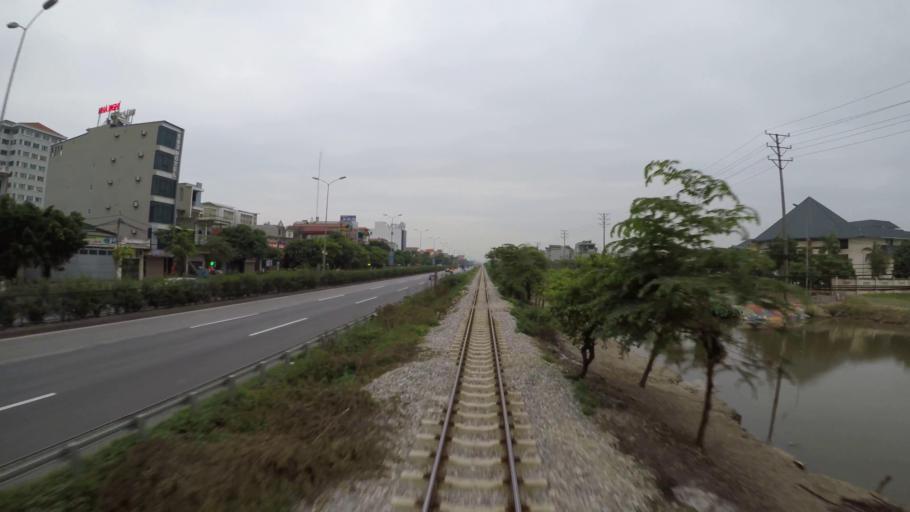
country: VN
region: Hung Yen
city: Nhu Quynh
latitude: 20.9835
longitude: 105.9792
